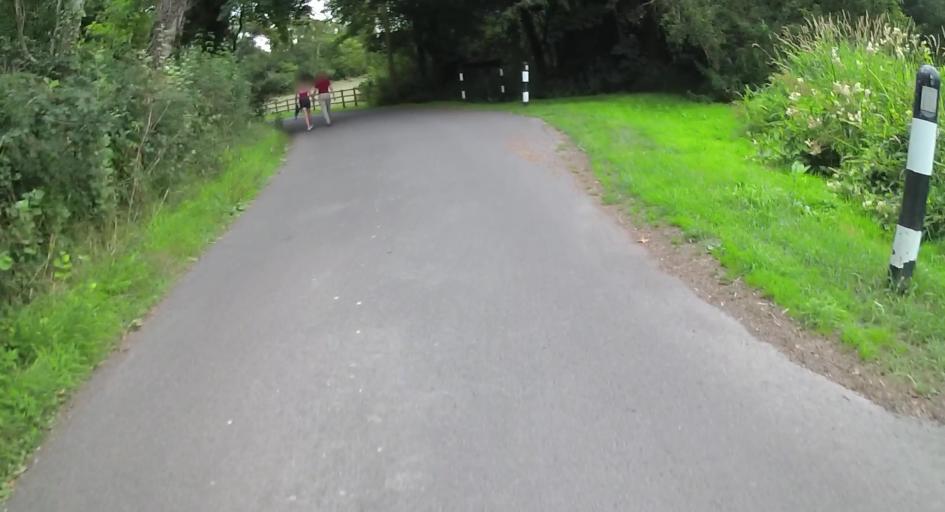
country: GB
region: England
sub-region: Hampshire
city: Kings Worthy
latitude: 51.1520
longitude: -1.3034
